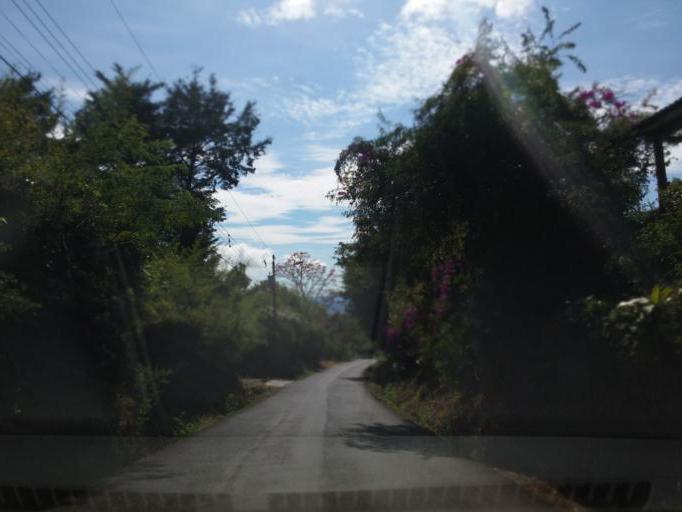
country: CR
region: Heredia
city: Santo Domingo
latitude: 10.0517
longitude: -84.1538
